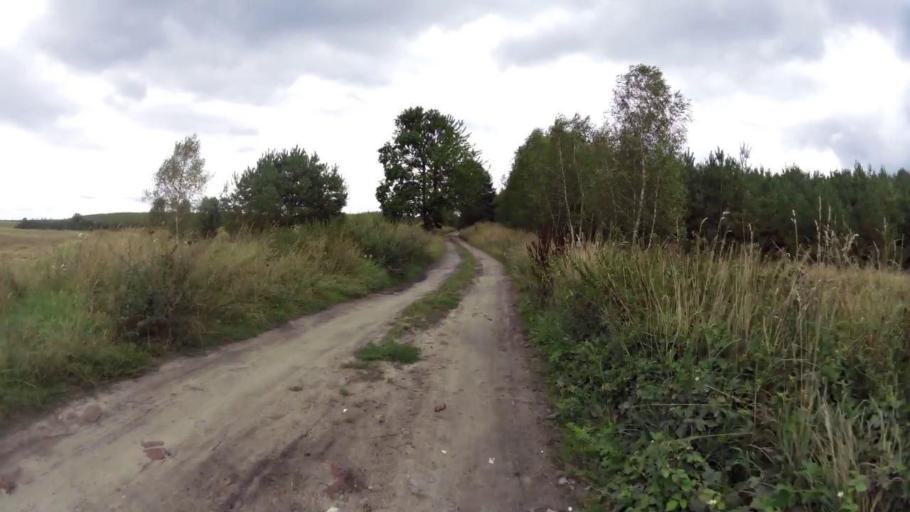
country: PL
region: West Pomeranian Voivodeship
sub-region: Powiat mysliborski
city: Debno
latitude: 52.7785
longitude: 14.7092
